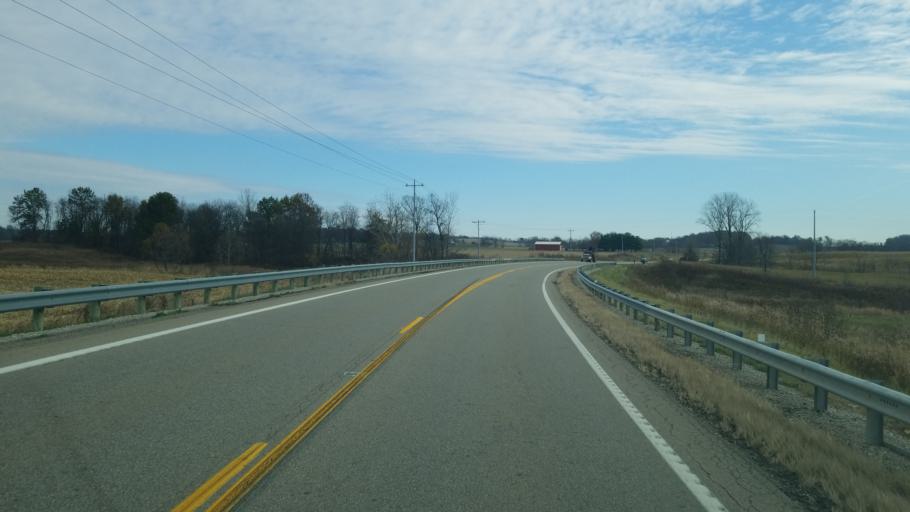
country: US
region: Ohio
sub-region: Licking County
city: Utica
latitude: 40.2306
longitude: -82.4973
